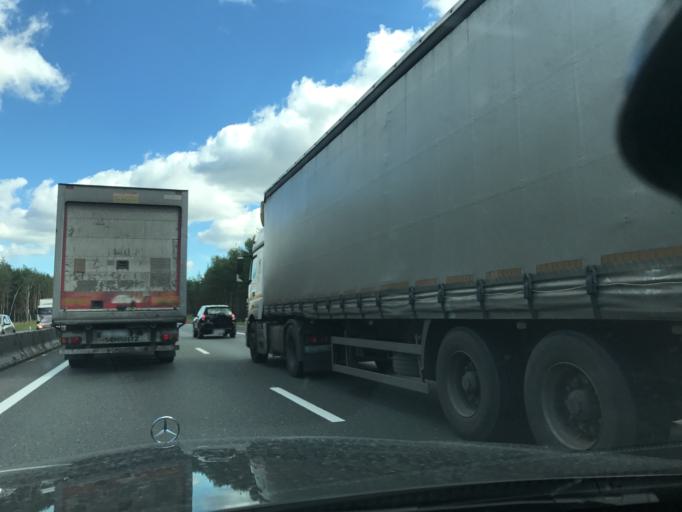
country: RU
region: Nizjnij Novgorod
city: Pyra
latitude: 56.2950
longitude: 43.3944
